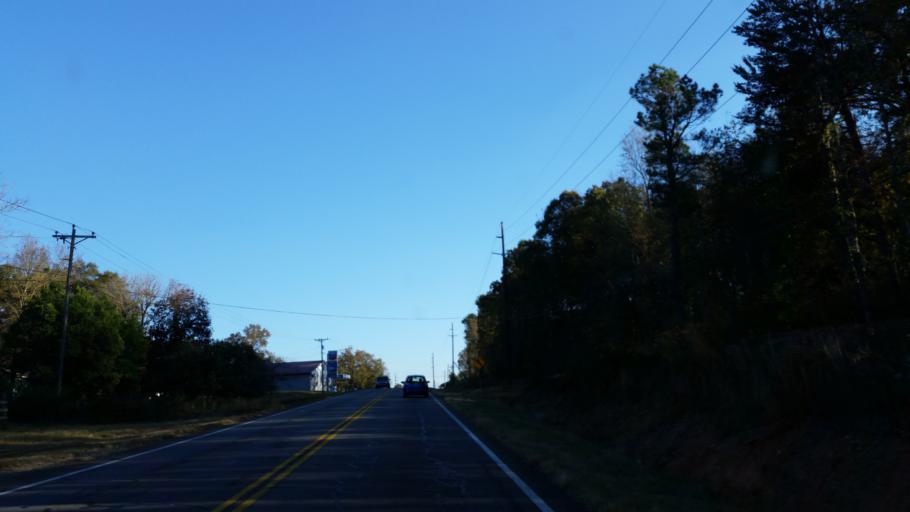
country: US
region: Georgia
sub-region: Gilmer County
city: Ellijay
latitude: 34.6465
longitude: -84.3917
